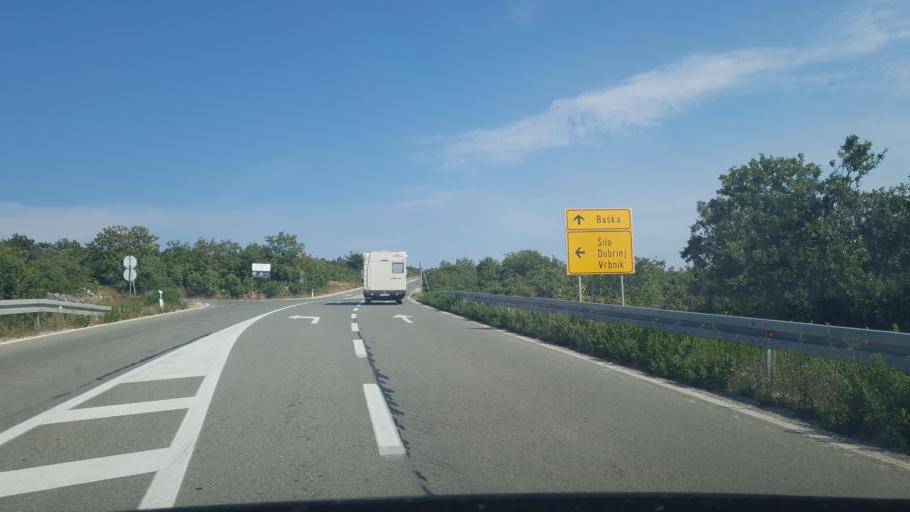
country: HR
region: Primorsko-Goranska
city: Punat
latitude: 45.0441
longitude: 14.6374
